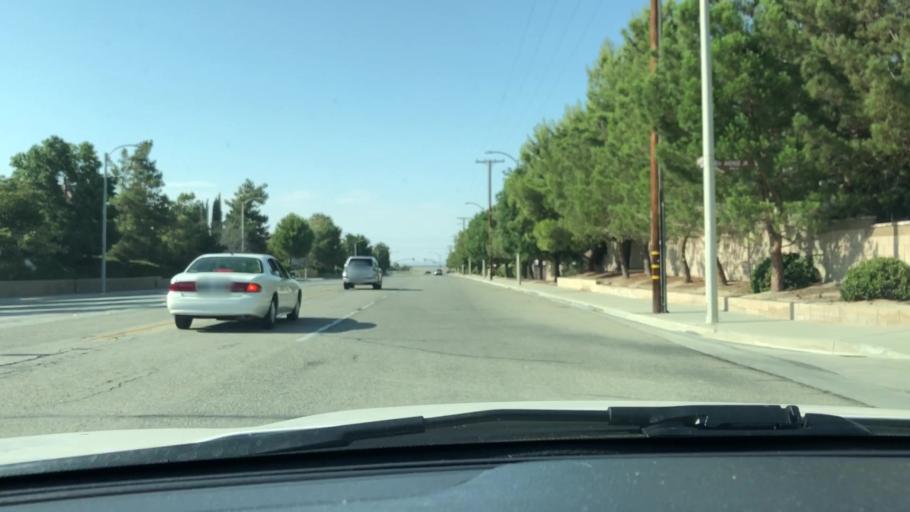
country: US
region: California
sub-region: Los Angeles County
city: Quartz Hill
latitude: 34.6858
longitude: -118.2014
